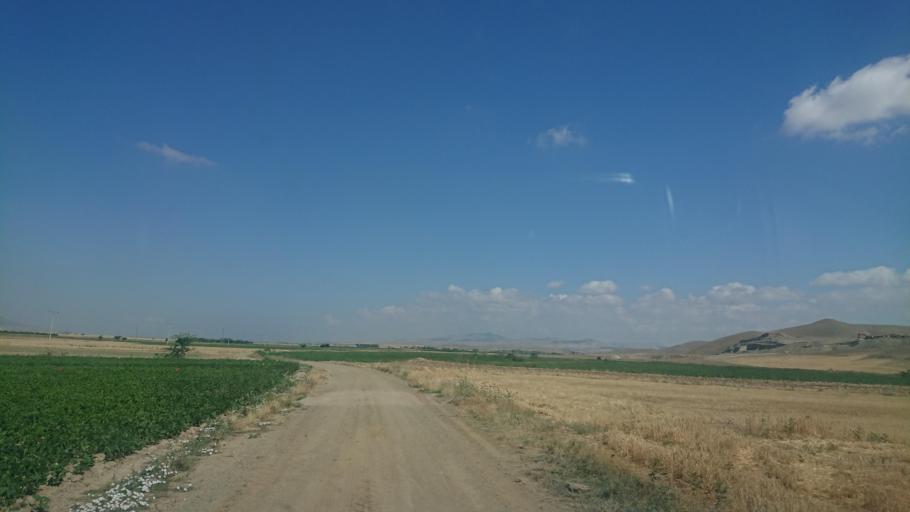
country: TR
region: Aksaray
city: Sariyahsi
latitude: 38.9758
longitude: 33.9133
